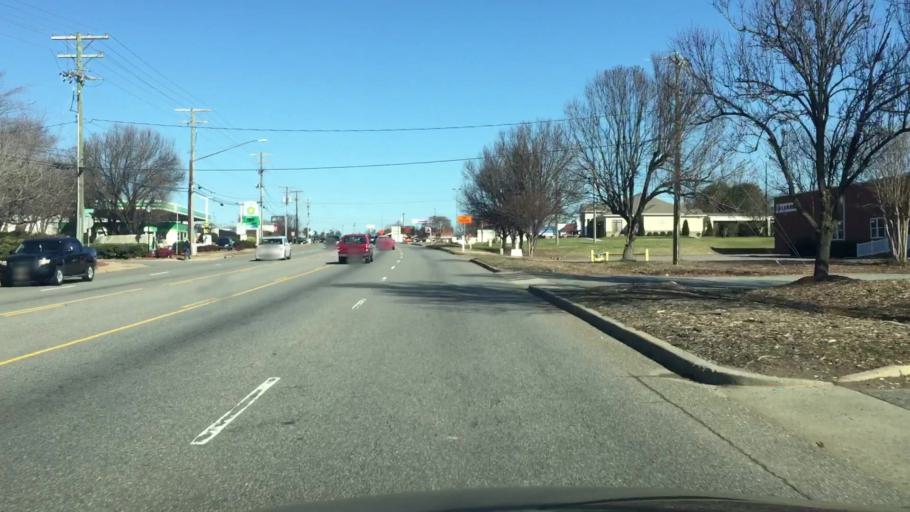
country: US
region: North Carolina
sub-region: Iredell County
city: Mooresville
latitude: 35.5964
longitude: -80.8152
